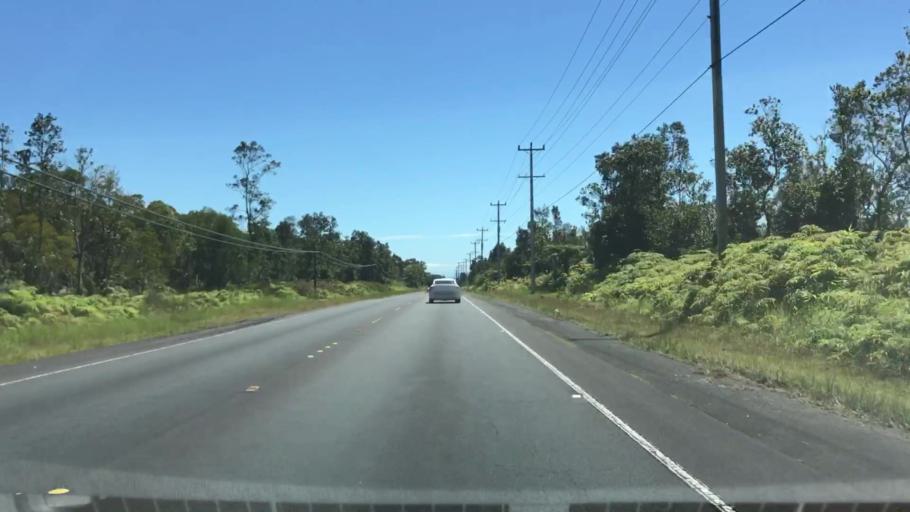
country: US
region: Hawaii
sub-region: Hawaii County
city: Volcano
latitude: 19.4534
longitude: -155.1809
